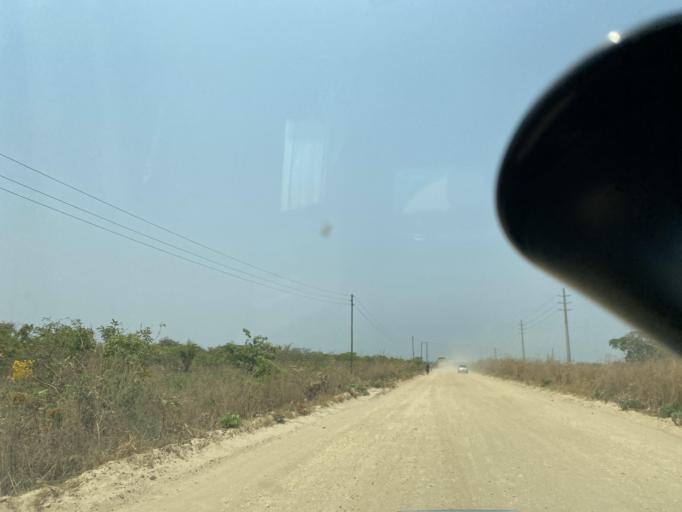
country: ZM
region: Lusaka
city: Lusaka
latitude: -15.5348
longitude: 28.3480
